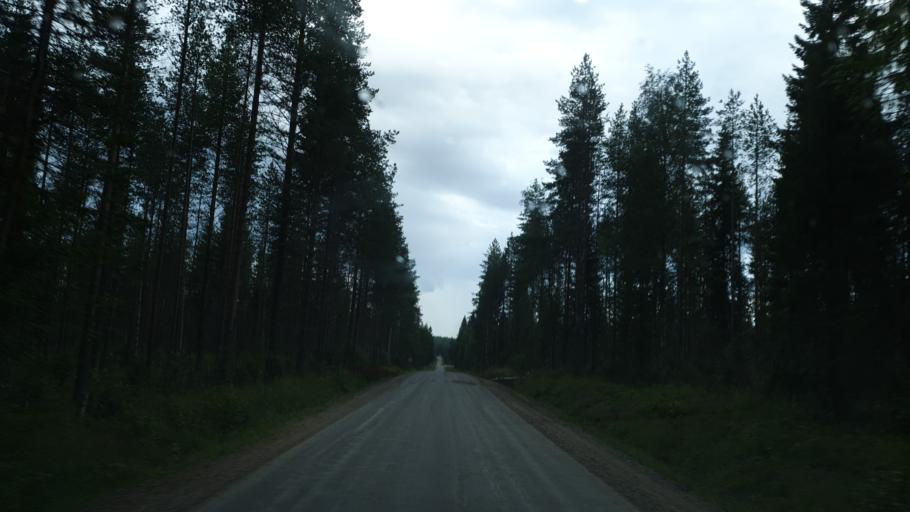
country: FI
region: Kainuu
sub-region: Kehys-Kainuu
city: Kuhmo
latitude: 64.2153
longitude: 29.3681
